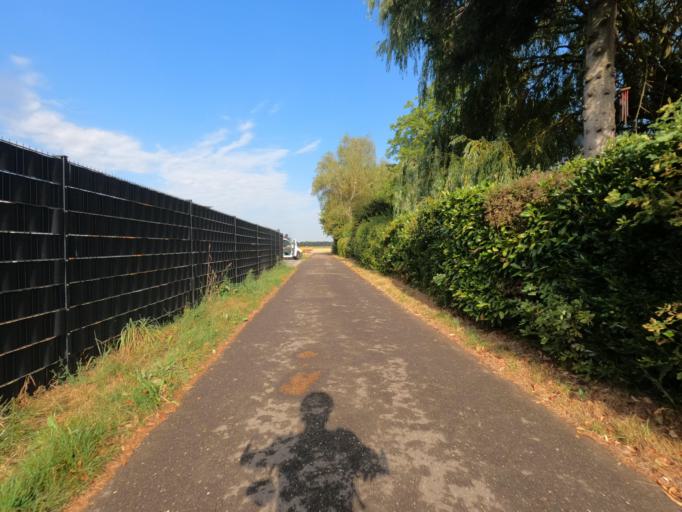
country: DE
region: North Rhine-Westphalia
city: Wegberg
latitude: 51.1037
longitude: 6.2497
